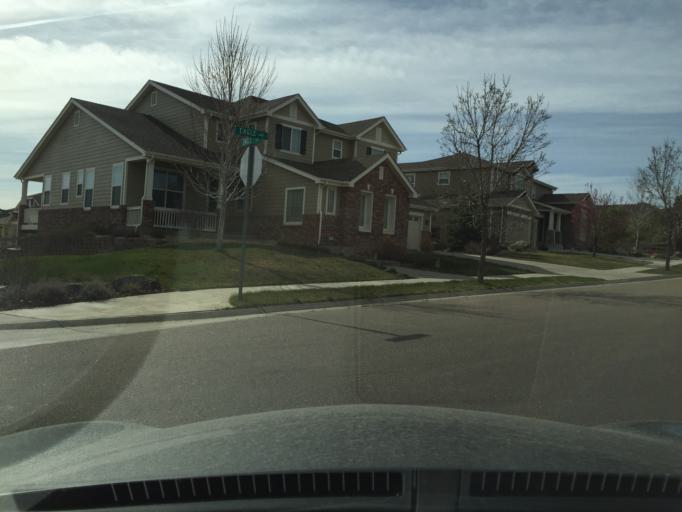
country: US
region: Colorado
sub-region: Boulder County
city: Erie
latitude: 40.0033
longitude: -105.0250
